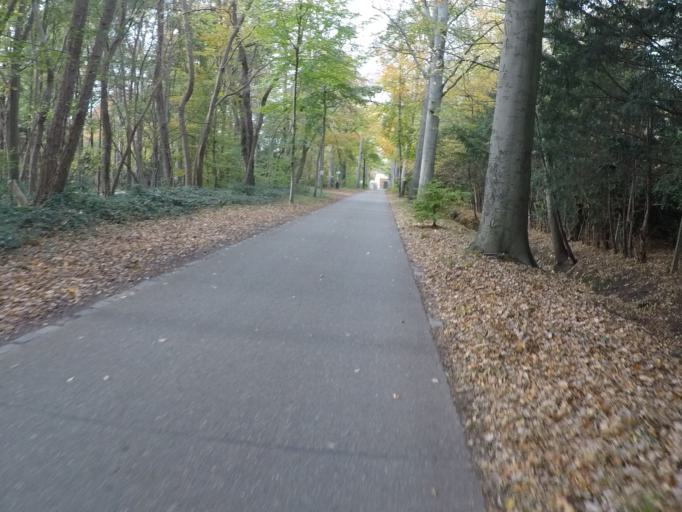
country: BE
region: Flanders
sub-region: Provincie Antwerpen
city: Lier
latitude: 51.1444
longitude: 4.5886
